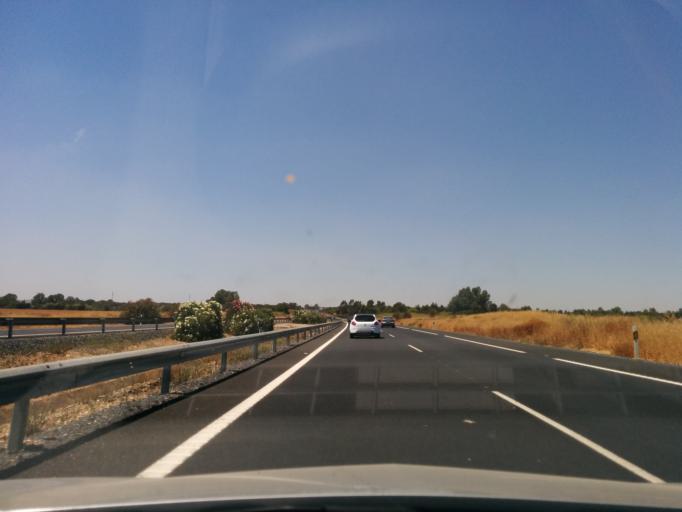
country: ES
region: Andalusia
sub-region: Provincia de Huelva
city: Lucena del Puerto
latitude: 37.3391
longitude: -6.7487
